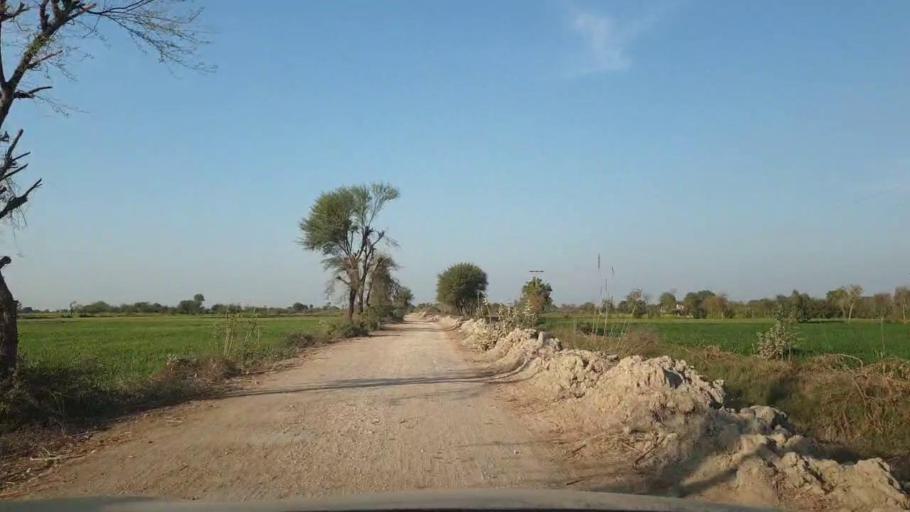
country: PK
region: Sindh
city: Tando Adam
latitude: 25.6956
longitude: 68.7023
